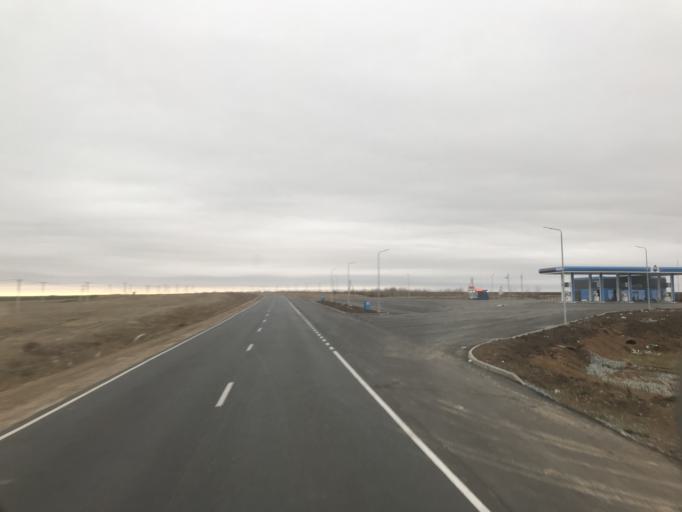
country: KZ
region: Batys Qazaqstan
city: Peremetnoe
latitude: 51.6480
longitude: 51.0121
